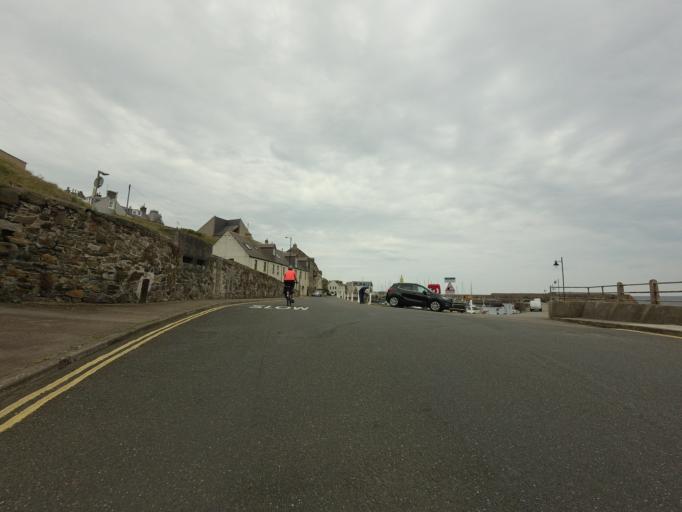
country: GB
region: Scotland
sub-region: Aberdeenshire
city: Banff
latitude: 57.6686
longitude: -2.5224
